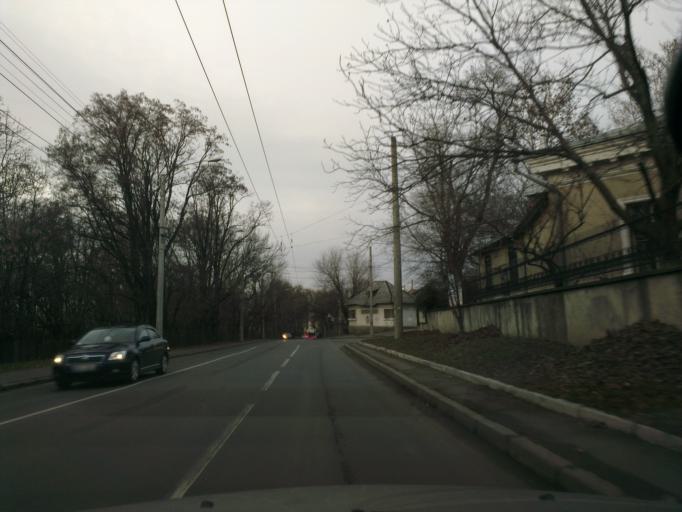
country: MD
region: Chisinau
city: Chisinau
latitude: 47.0305
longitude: 28.8169
